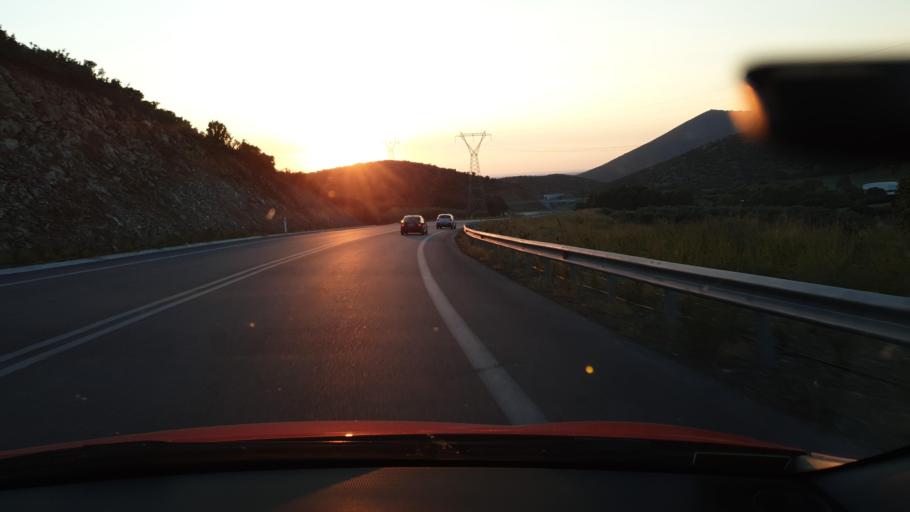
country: GR
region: Central Macedonia
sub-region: Nomos Chalkidikis
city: Galatista
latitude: 40.4640
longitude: 23.2169
